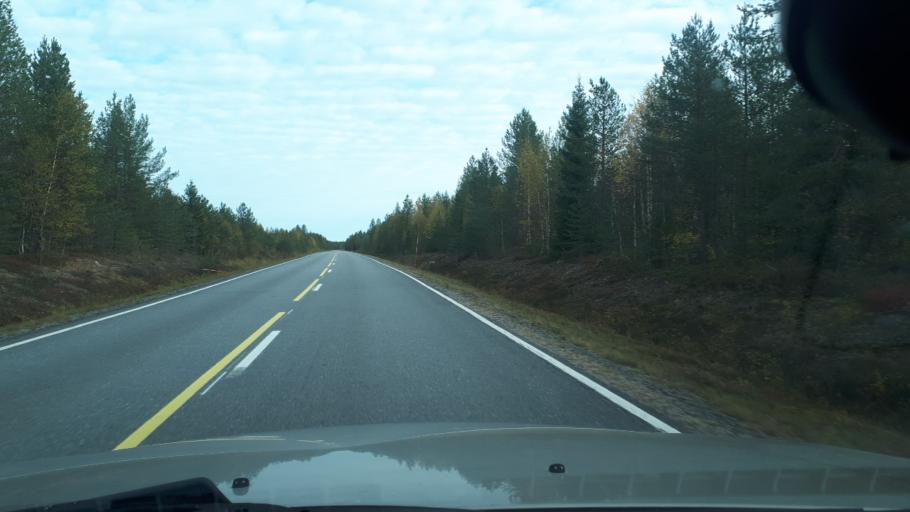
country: FI
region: Northern Ostrobothnia
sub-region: Oulu
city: Yli-Ii
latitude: 65.9030
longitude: 25.7343
